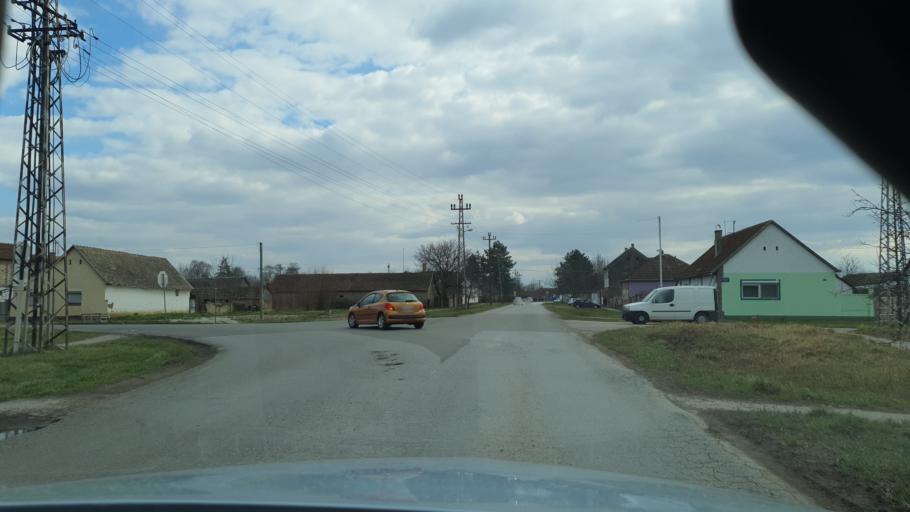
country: RS
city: Maglic
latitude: 45.3896
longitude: 19.4598
